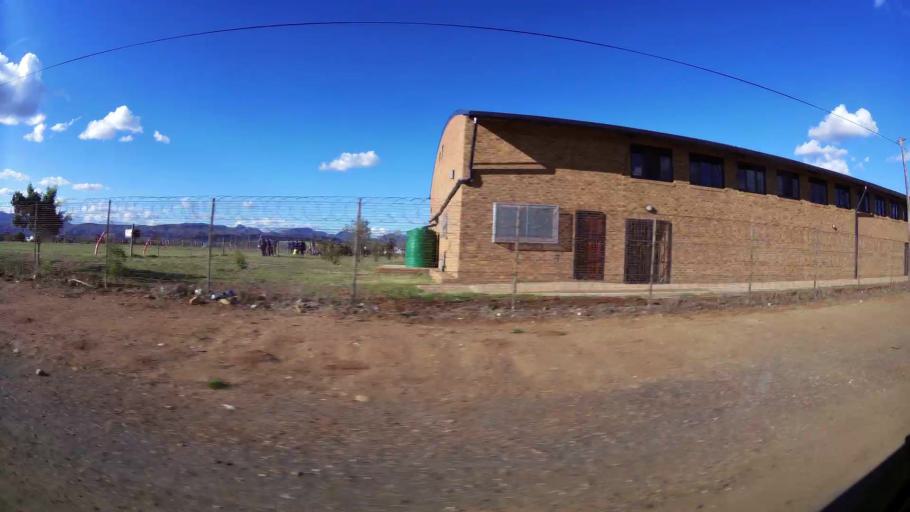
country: ZA
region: Western Cape
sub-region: Eden District Municipality
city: Riversdale
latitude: -34.1063
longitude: 20.9558
